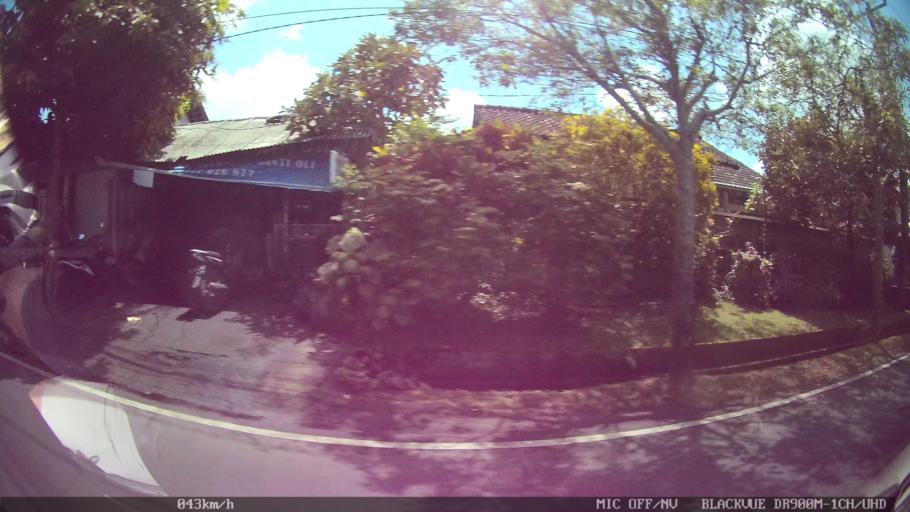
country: ID
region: Bali
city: Banjar Jabejero
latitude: -8.5922
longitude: 115.2628
